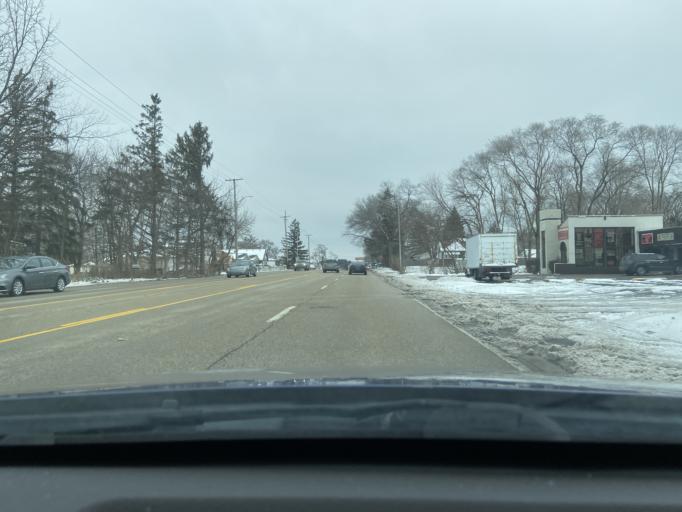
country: US
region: Illinois
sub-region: Lake County
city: Round Lake Beach
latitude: 42.3748
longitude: -88.0897
